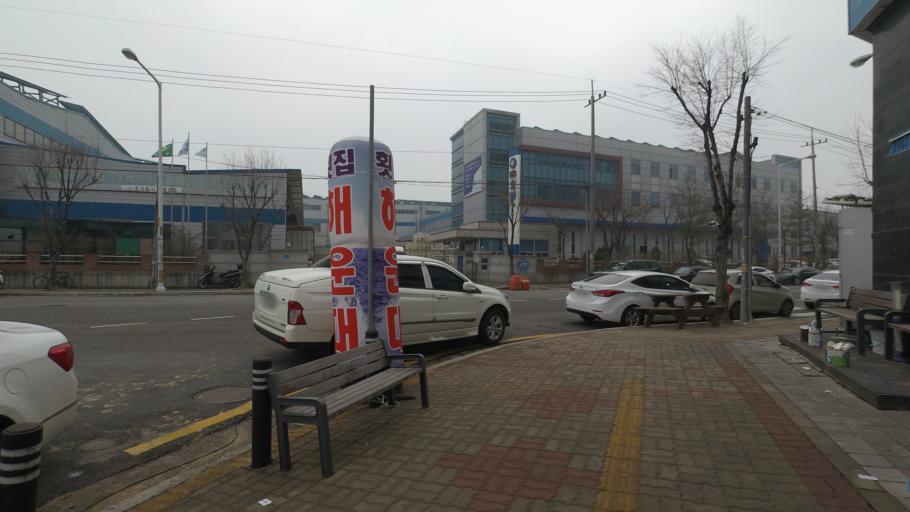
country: KR
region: Chungcheongnam-do
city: Tangjin
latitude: 36.9773
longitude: 126.8437
